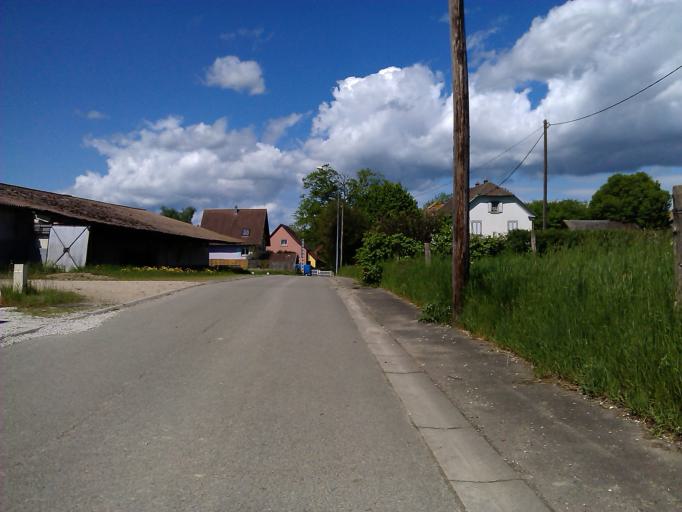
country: FR
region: Franche-Comte
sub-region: Territoire de Belfort
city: Montreux-Chateau
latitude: 47.6237
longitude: 7.0542
